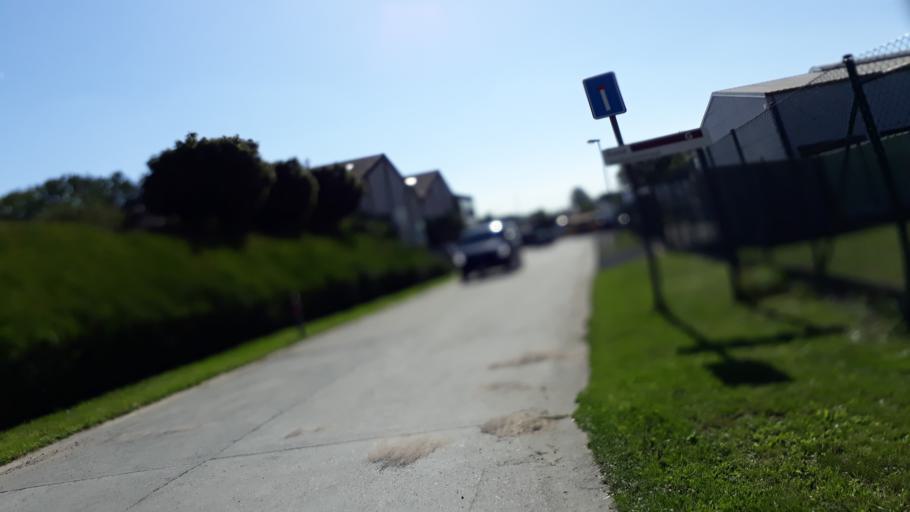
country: BE
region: Flanders
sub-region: Provincie West-Vlaanderen
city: Torhout
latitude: 51.0780
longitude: 3.1086
